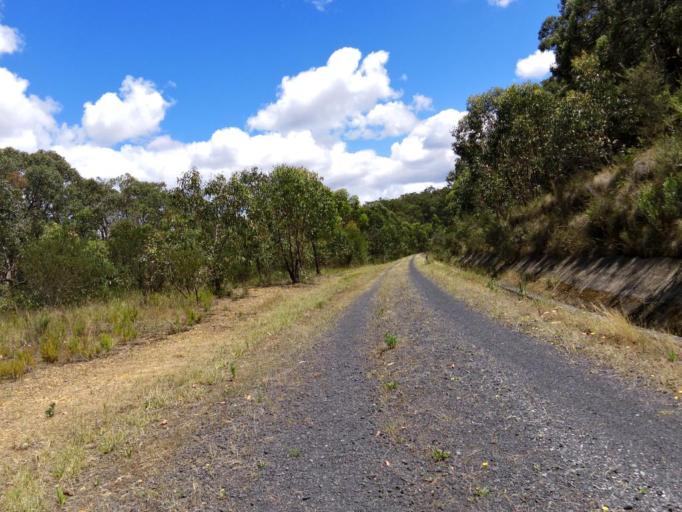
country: AU
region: Victoria
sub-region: Cardinia
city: Officer
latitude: -38.0356
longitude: 145.4195
